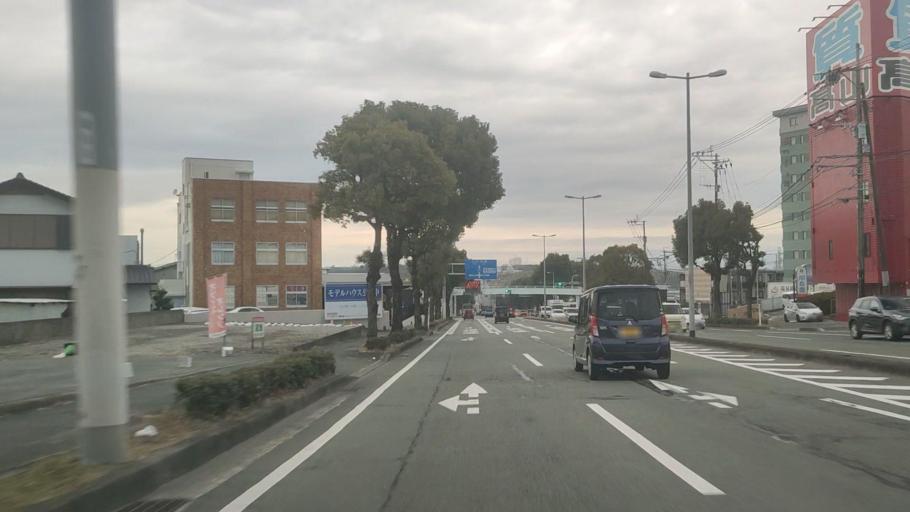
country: JP
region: Kumamoto
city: Ozu
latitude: 32.8414
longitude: 130.7803
